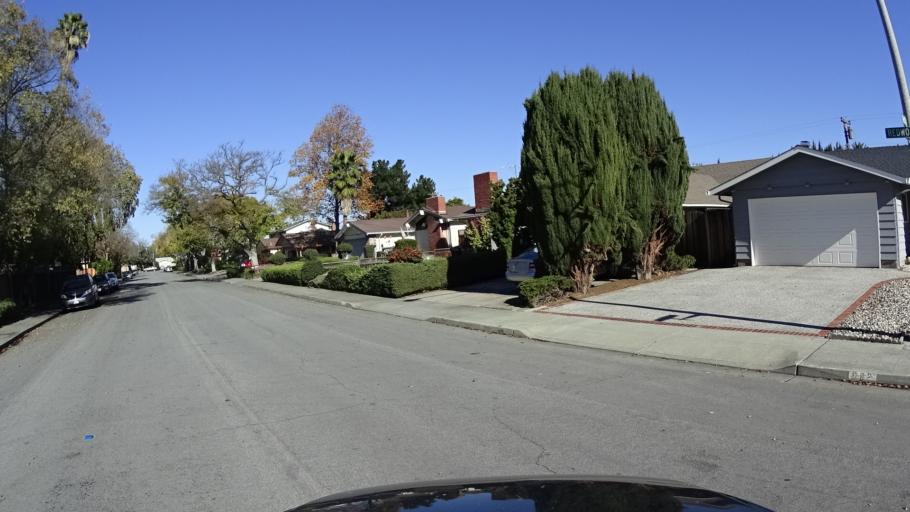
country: US
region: California
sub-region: Santa Clara County
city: Sunnyvale
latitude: 37.3560
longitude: -122.0060
